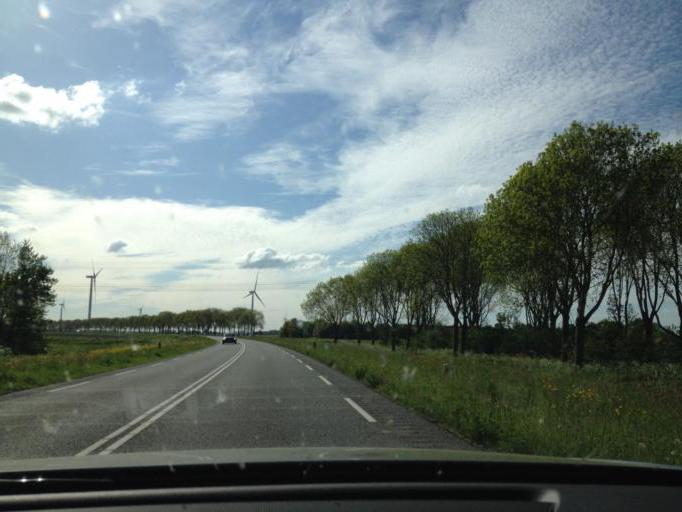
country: NL
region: Utrecht
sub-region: Gemeente Bunschoten
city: Bunschoten
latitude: 52.2807
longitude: 5.4372
